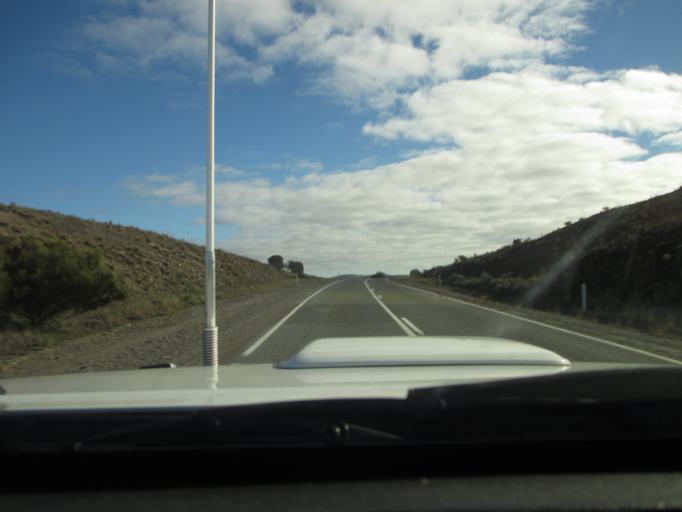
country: AU
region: South Australia
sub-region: Peterborough
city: Peterborough
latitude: -32.6116
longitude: 138.5714
